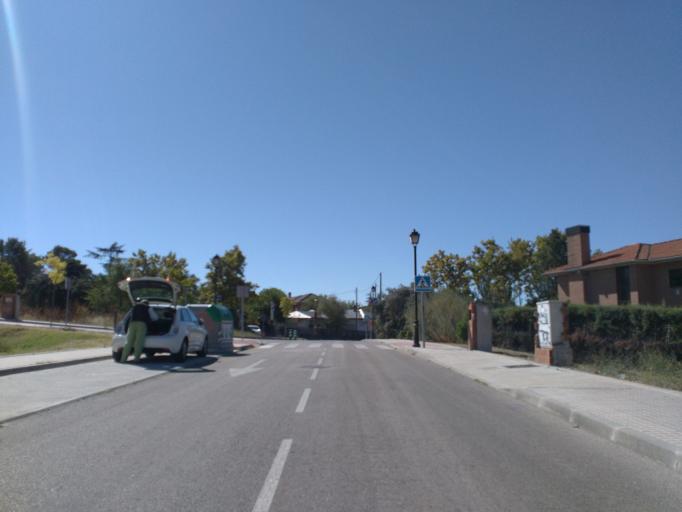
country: ES
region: Madrid
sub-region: Provincia de Madrid
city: Torrelodones
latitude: 40.5775
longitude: -3.9482
